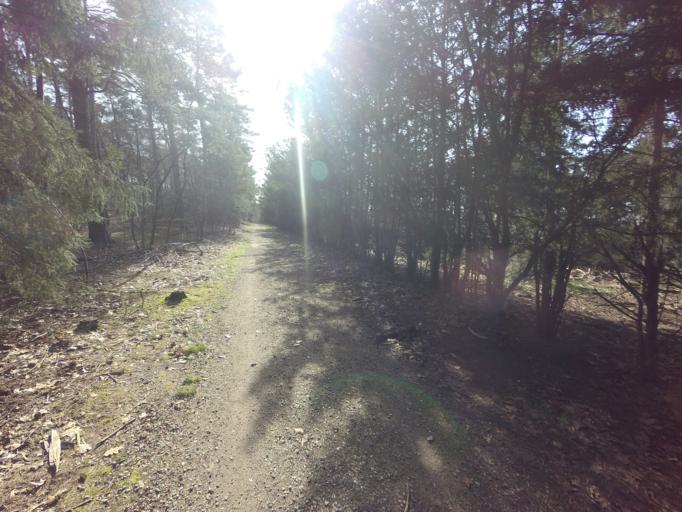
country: DE
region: North Rhine-Westphalia
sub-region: Regierungsbezirk Koln
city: Wassenberg
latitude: 51.1567
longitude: 6.1632
